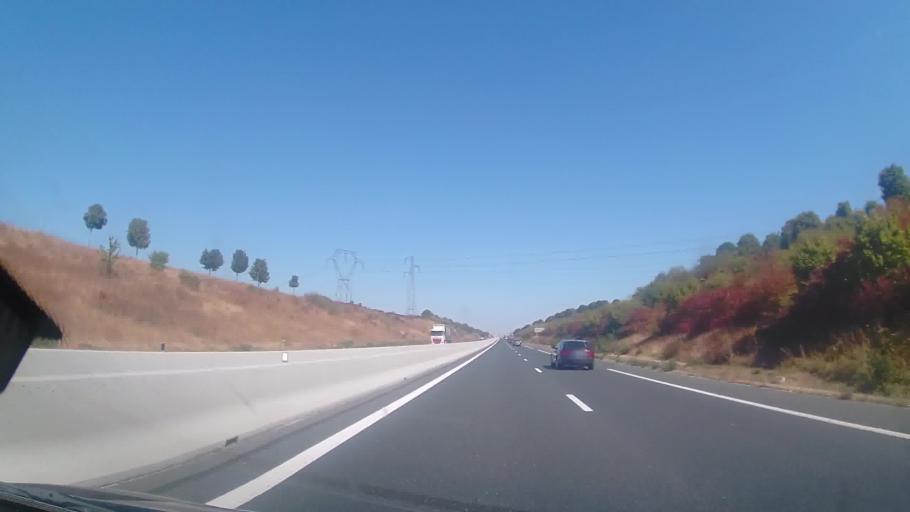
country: FR
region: Centre
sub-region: Departement de l'Indre
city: Saint-Maur
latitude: 46.8315
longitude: 1.6508
